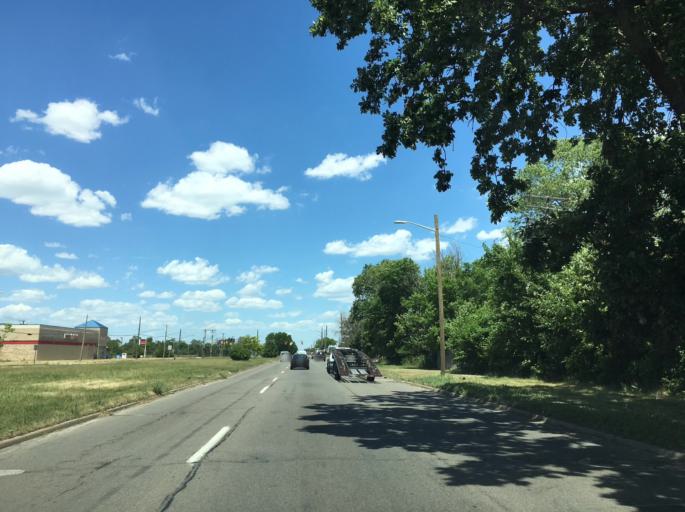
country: US
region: Michigan
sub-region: Macomb County
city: Warren
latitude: 42.4389
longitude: -83.0436
